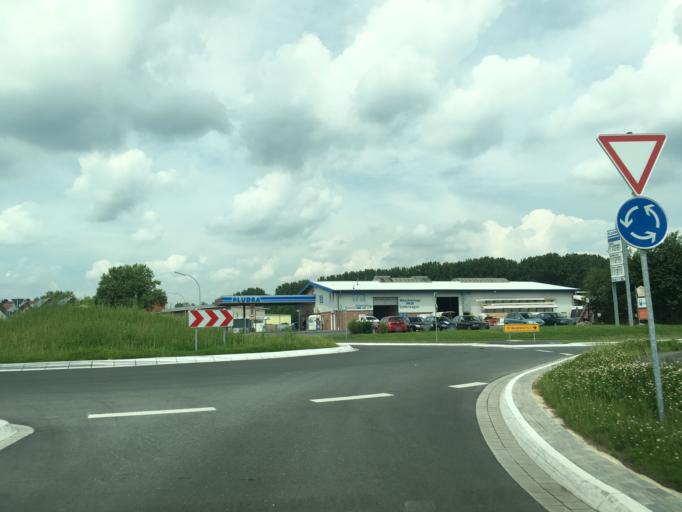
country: DE
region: North Rhine-Westphalia
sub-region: Regierungsbezirk Munster
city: Laer
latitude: 52.0603
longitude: 7.3692
